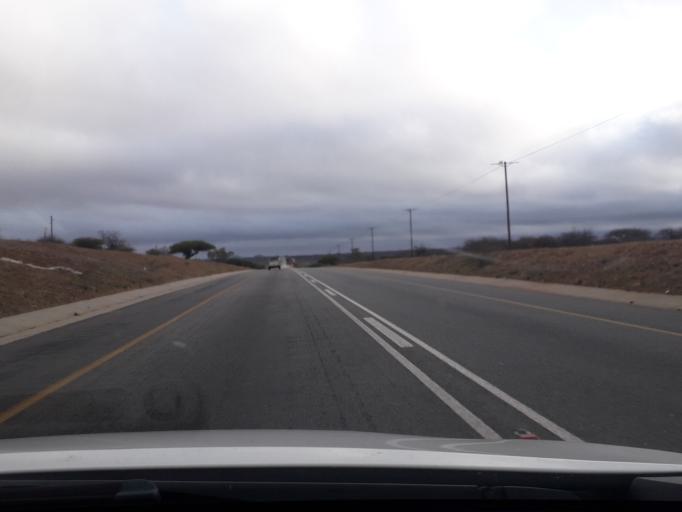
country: ZA
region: Limpopo
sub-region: Capricorn District Municipality
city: Polokwane
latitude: -23.6359
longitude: 29.6300
